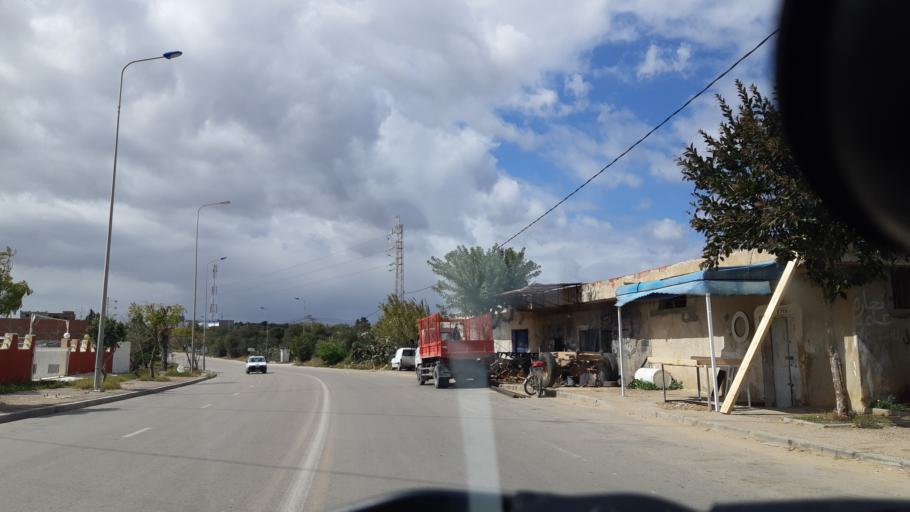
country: TN
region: Susah
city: Akouda
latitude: 35.8795
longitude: 10.5130
